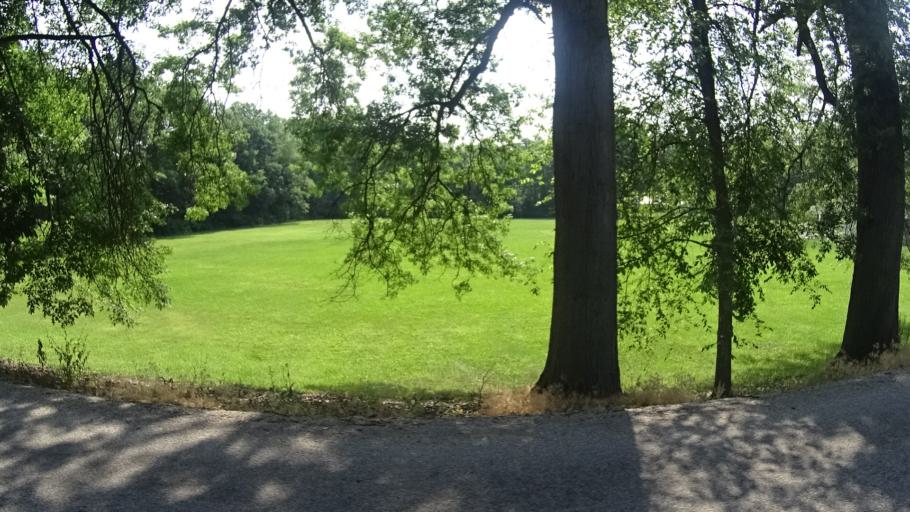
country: US
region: Ohio
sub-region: Lorain County
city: Vermilion
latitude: 41.3790
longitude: -82.4309
